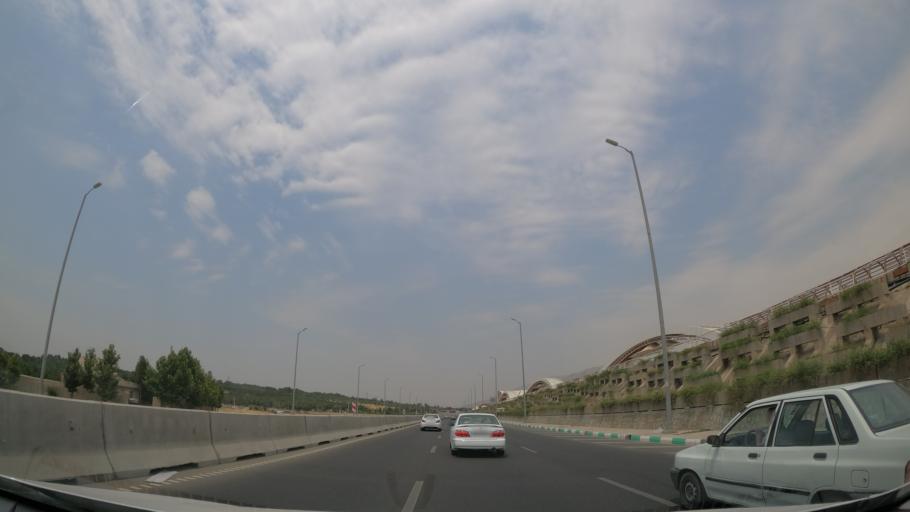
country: IR
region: Tehran
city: Shahr-e Qods
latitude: 35.7391
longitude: 51.2177
